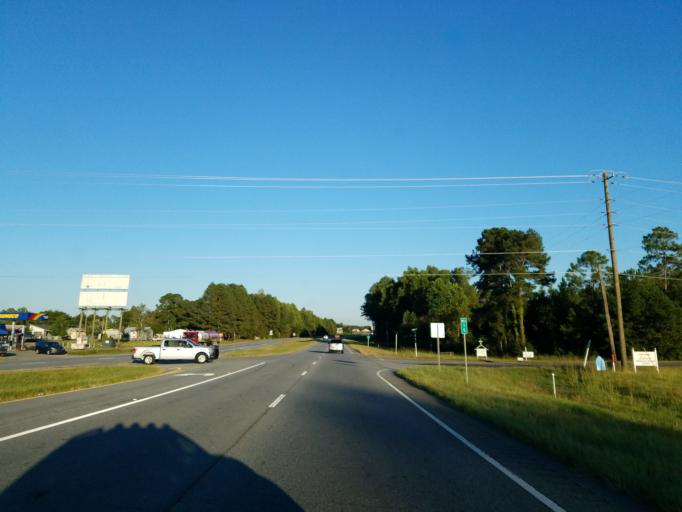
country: US
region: Georgia
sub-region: Worth County
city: Sylvester
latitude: 31.5084
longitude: -83.7397
